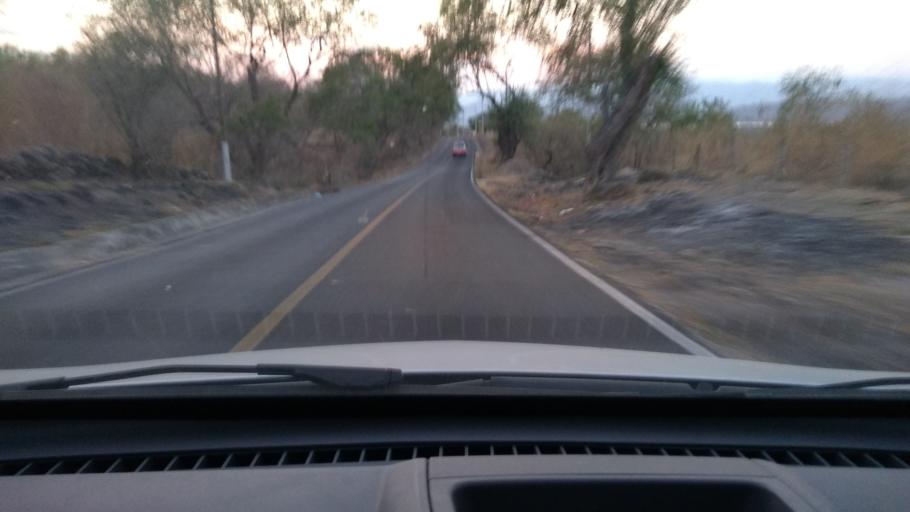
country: MX
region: Morelos
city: Coatetelco
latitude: 18.7215
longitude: -99.3092
